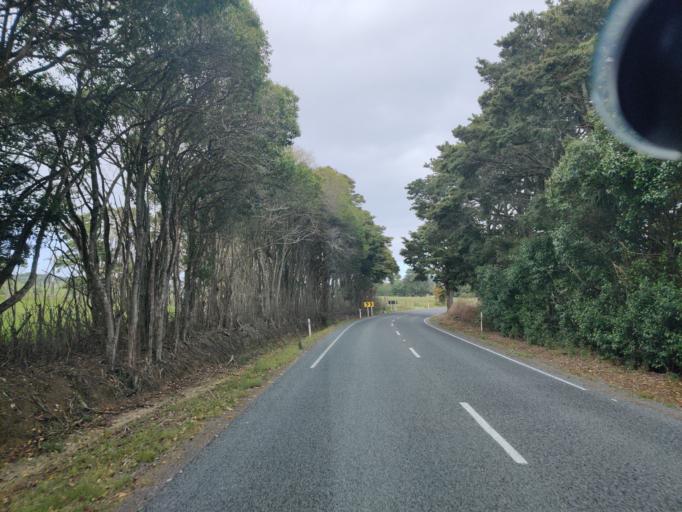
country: NZ
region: Northland
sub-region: Whangarei
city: Ngunguru
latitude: -35.5633
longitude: 174.3872
